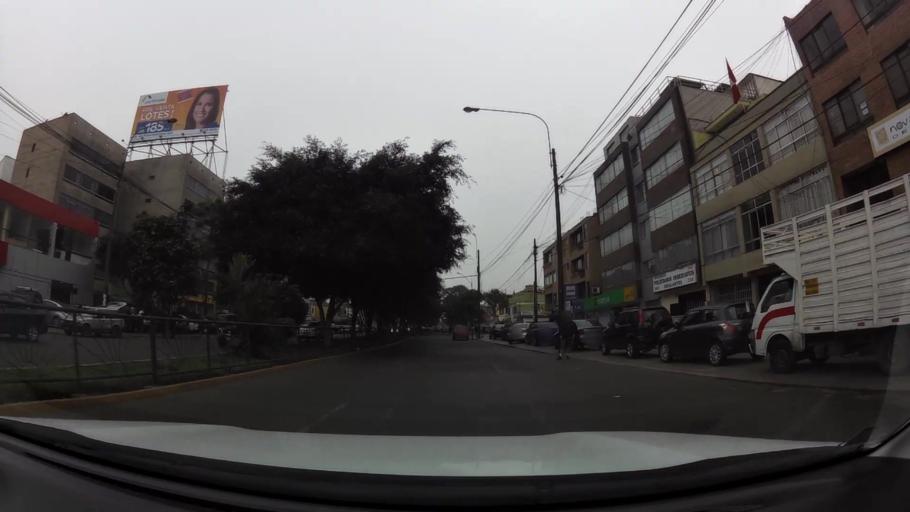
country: PE
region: Lima
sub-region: Lima
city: Surco
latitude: -12.1287
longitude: -76.9978
